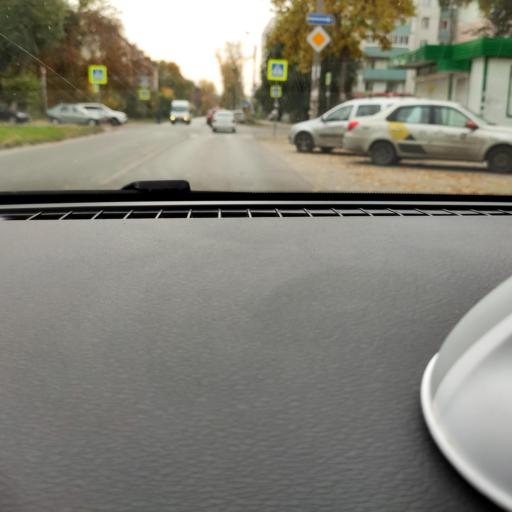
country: RU
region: Samara
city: Petra-Dubrava
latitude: 53.2293
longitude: 50.2739
